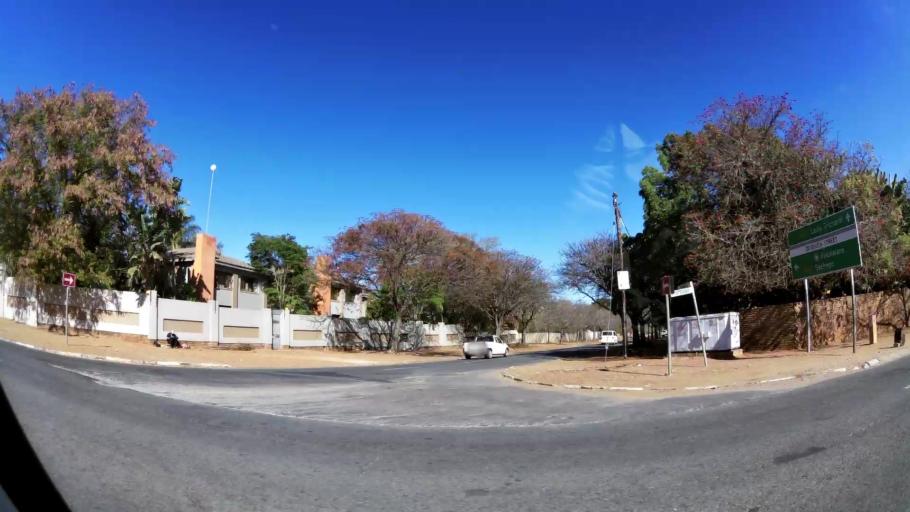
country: ZA
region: Limpopo
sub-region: Capricorn District Municipality
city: Polokwane
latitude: -23.9008
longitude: 29.4716
